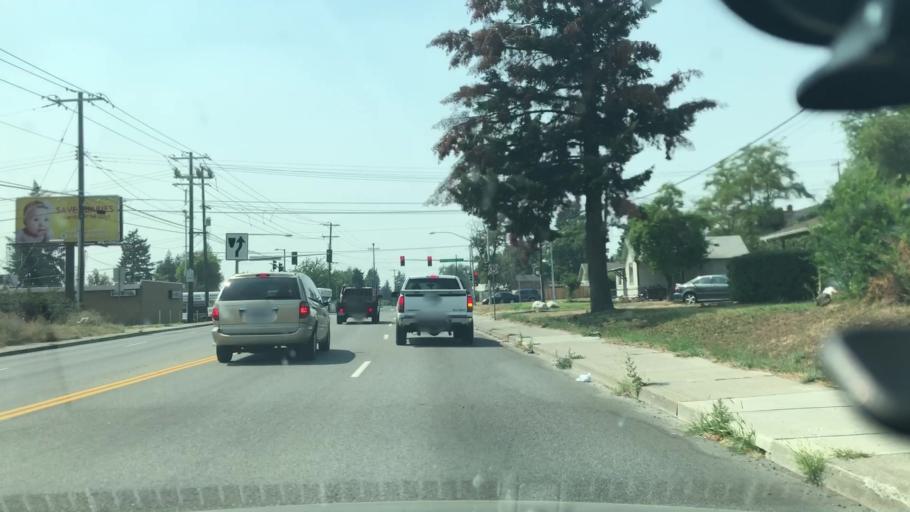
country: US
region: Washington
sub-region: Spokane County
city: Spokane
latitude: 47.6863
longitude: -117.3777
